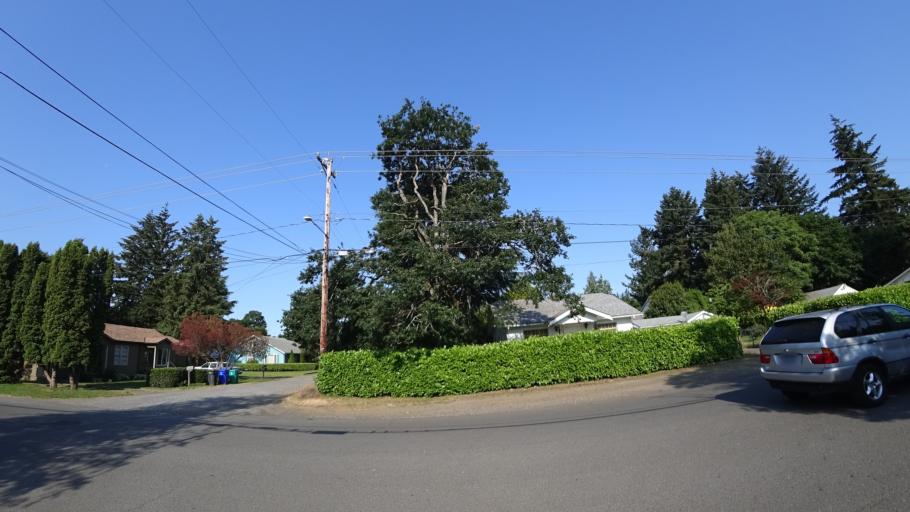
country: US
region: Oregon
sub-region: Multnomah County
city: Lents
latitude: 45.4632
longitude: -122.5996
